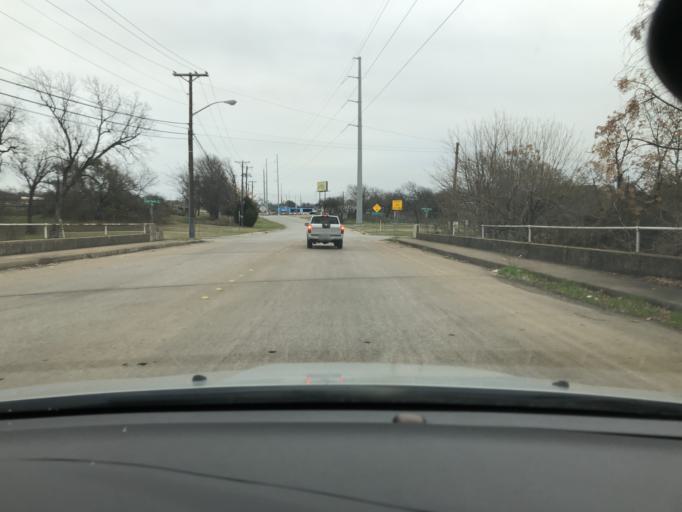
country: US
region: Texas
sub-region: Tarrant County
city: Fort Worth
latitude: 32.7267
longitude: -97.2939
